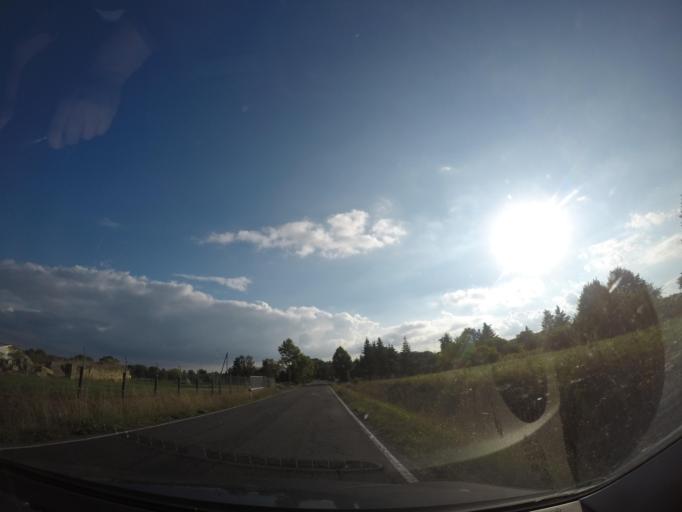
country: DE
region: Saxony-Anhalt
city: Weferlingen
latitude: 52.3213
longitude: 11.0625
